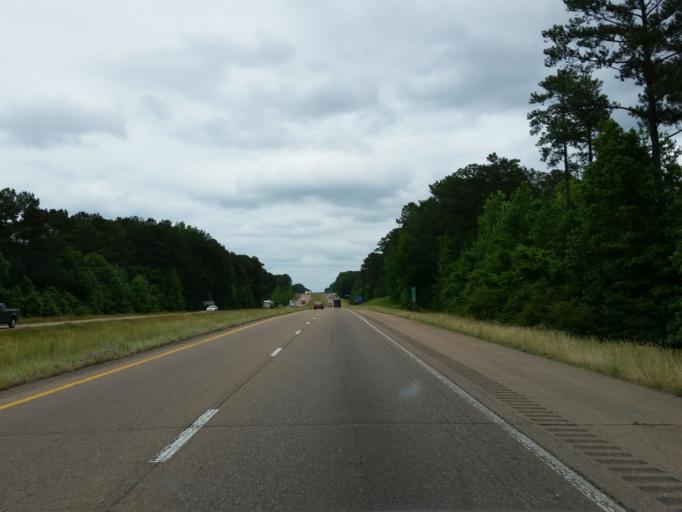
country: US
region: Mississippi
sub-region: Lauderdale County
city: Marion
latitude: 32.3914
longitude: -88.5942
